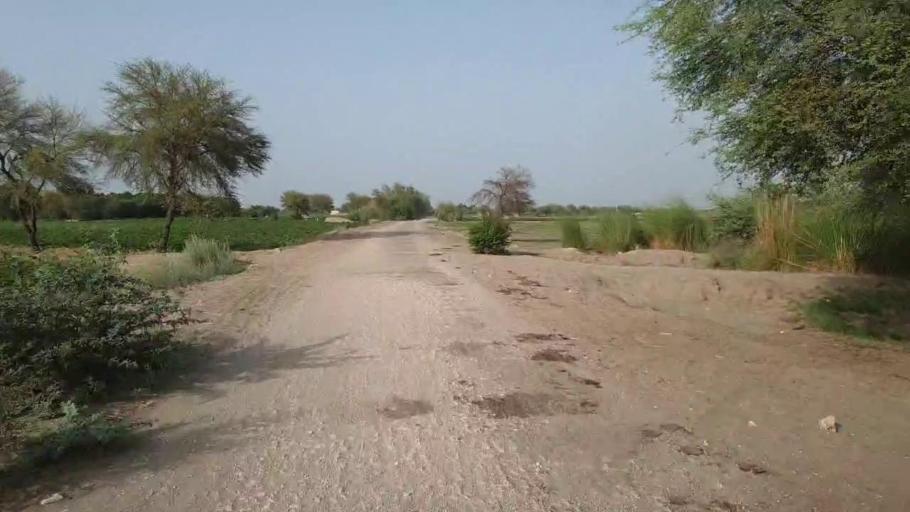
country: PK
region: Sindh
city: Daur
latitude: 26.3420
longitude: 68.2606
